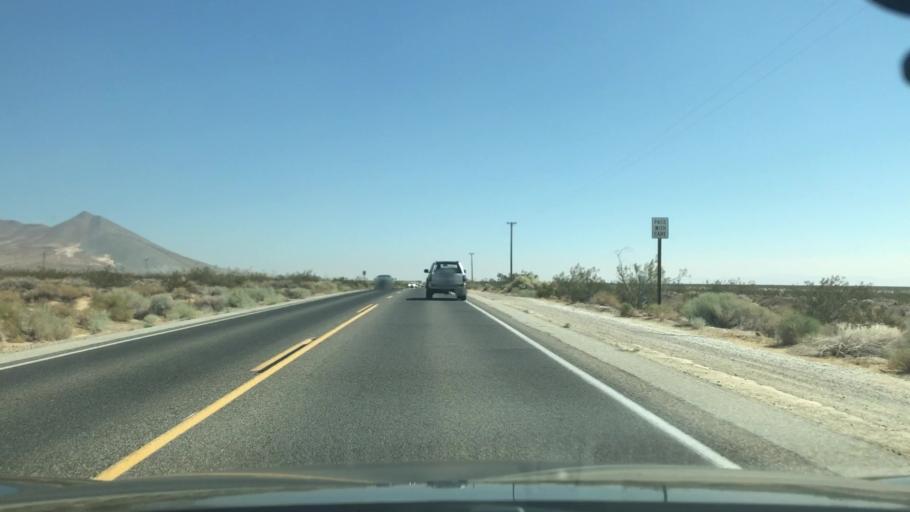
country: US
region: California
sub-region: Kern County
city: Inyokern
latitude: 35.5698
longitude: -117.9177
